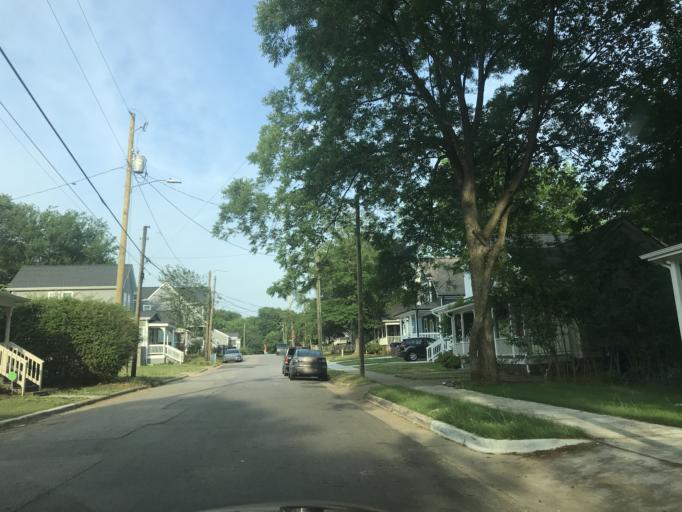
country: US
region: North Carolina
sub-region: Wake County
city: Raleigh
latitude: 35.7740
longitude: -78.6293
